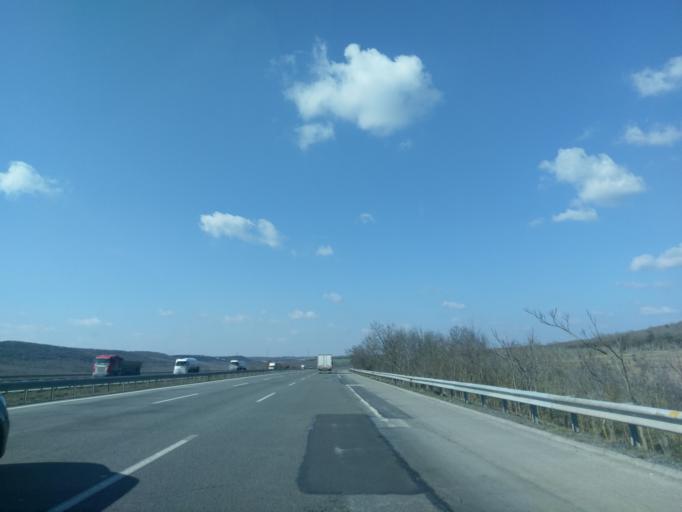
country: TR
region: Istanbul
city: Canta
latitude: 41.1688
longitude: 28.1231
